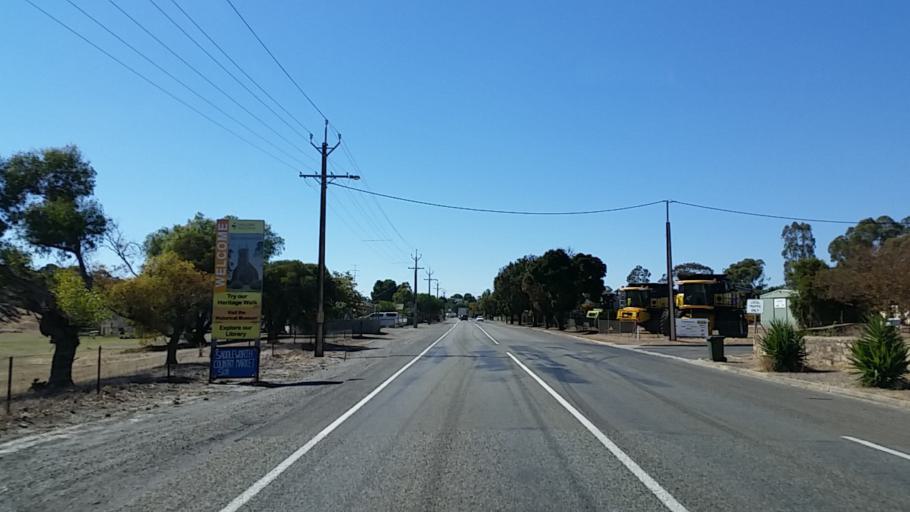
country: AU
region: South Australia
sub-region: Light
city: Kapunda
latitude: -34.0869
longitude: 138.7770
